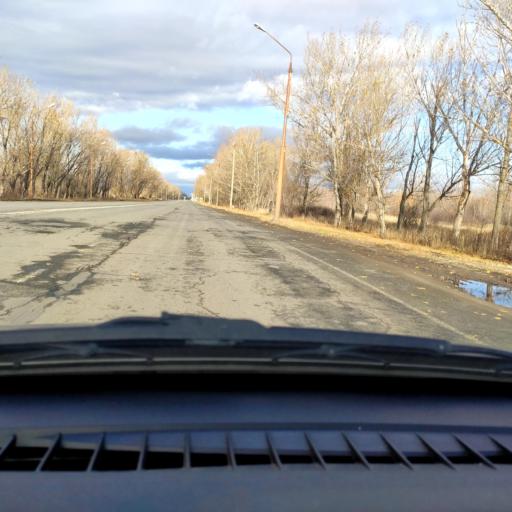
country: RU
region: Samara
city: Podstepki
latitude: 53.5618
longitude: 49.2159
